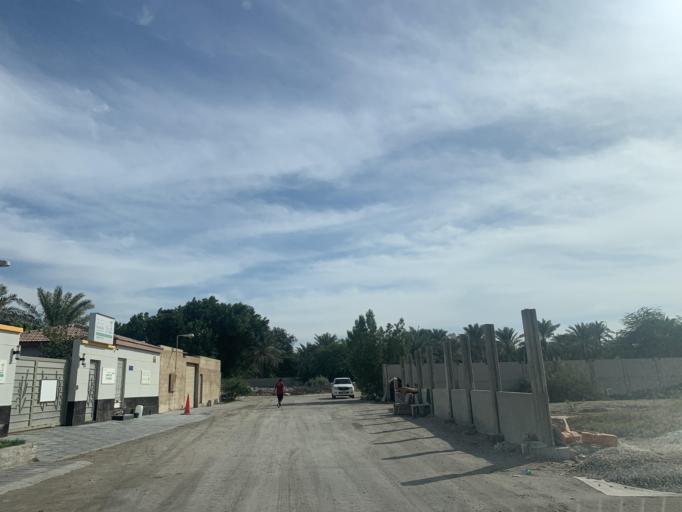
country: BH
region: Central Governorate
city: Madinat Hamad
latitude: 26.1230
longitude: 50.4692
